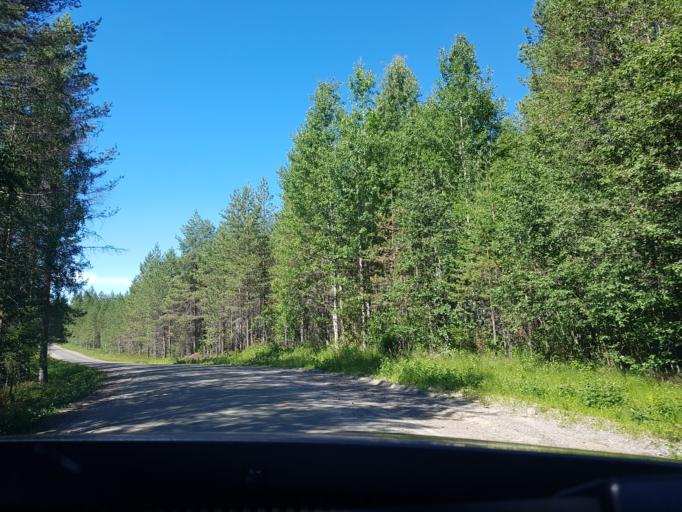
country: FI
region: Kainuu
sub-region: Kehys-Kainuu
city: Kuhmo
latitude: 64.1950
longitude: 29.6021
